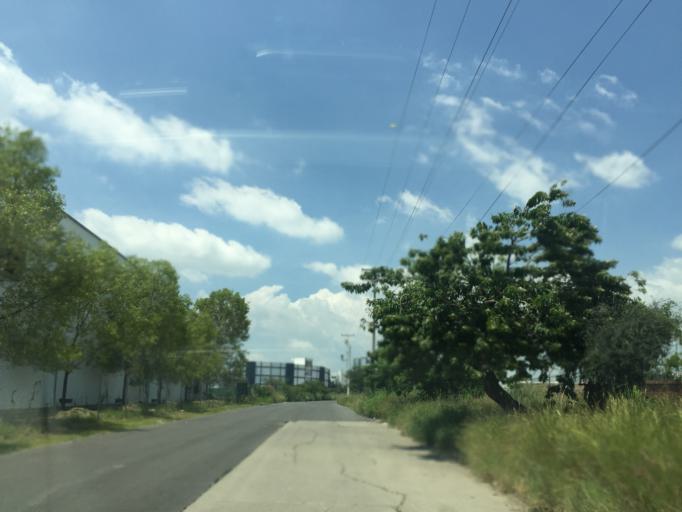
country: MX
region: Guanajuato
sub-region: Leon
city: La Ermita
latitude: 21.1528
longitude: -101.7174
